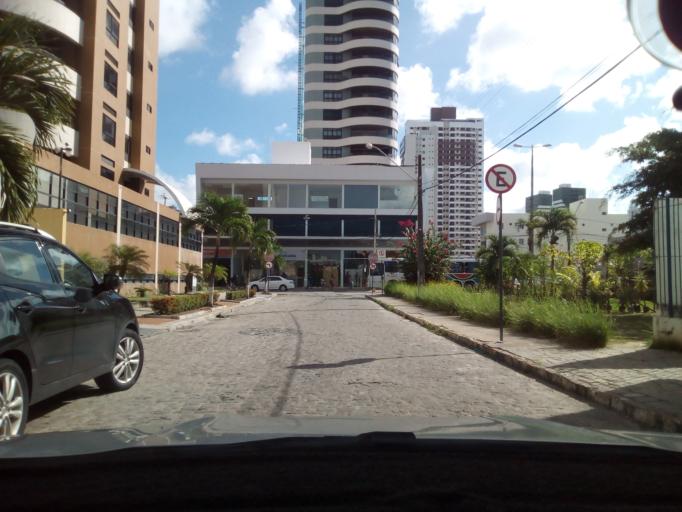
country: BR
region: Paraiba
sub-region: Joao Pessoa
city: Joao Pessoa
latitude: -7.1112
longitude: -34.8285
